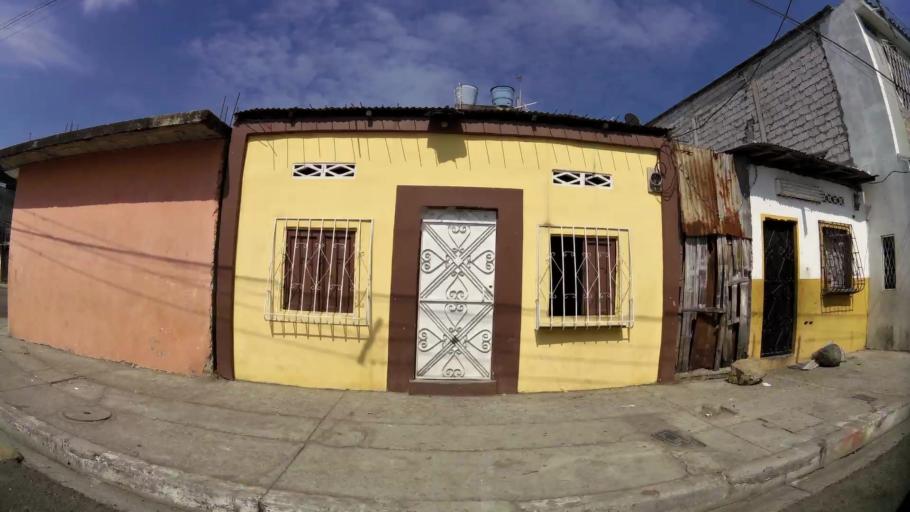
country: EC
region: Guayas
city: Guayaquil
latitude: -2.2798
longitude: -79.8787
